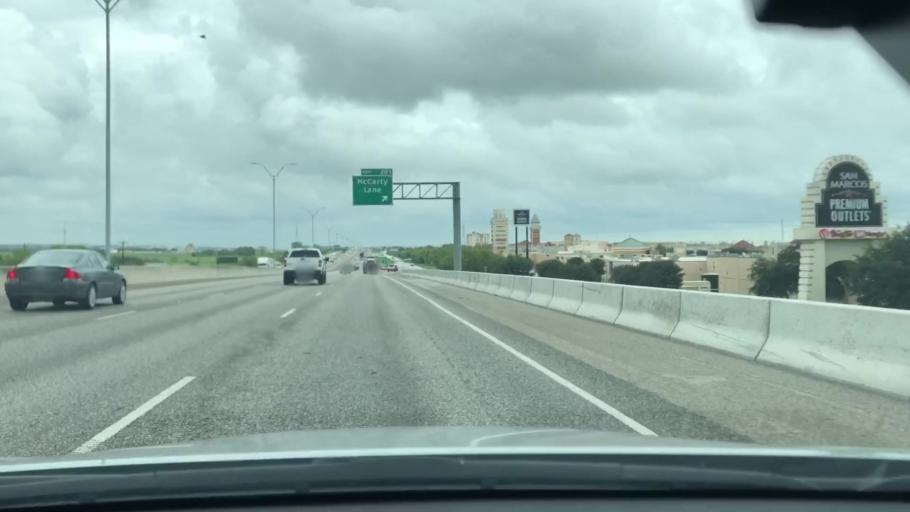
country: US
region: Texas
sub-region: Hays County
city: San Marcos
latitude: 29.8276
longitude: -97.9884
